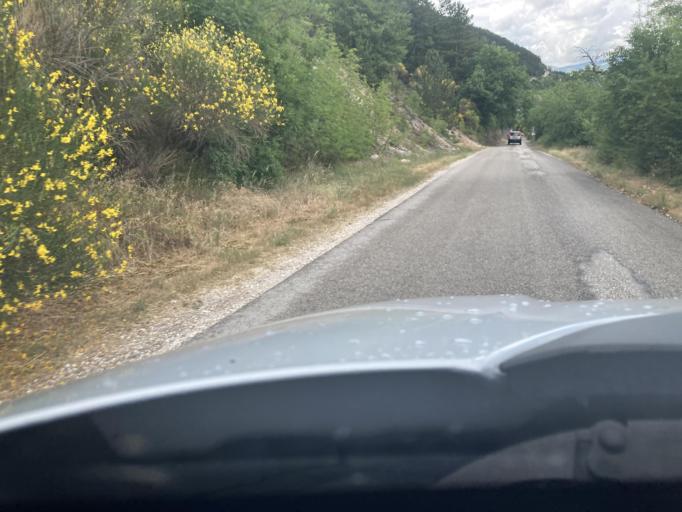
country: IT
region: Abruzzo
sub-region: Provincia dell' Aquila
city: Fossa
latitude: 42.2891
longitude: 13.4907
